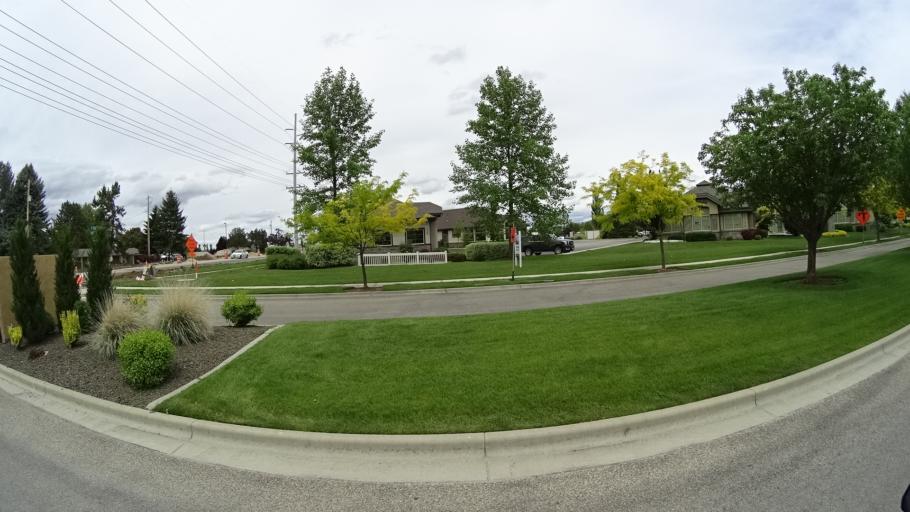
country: US
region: Idaho
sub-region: Ada County
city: Meridian
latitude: 43.6436
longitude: -116.4333
